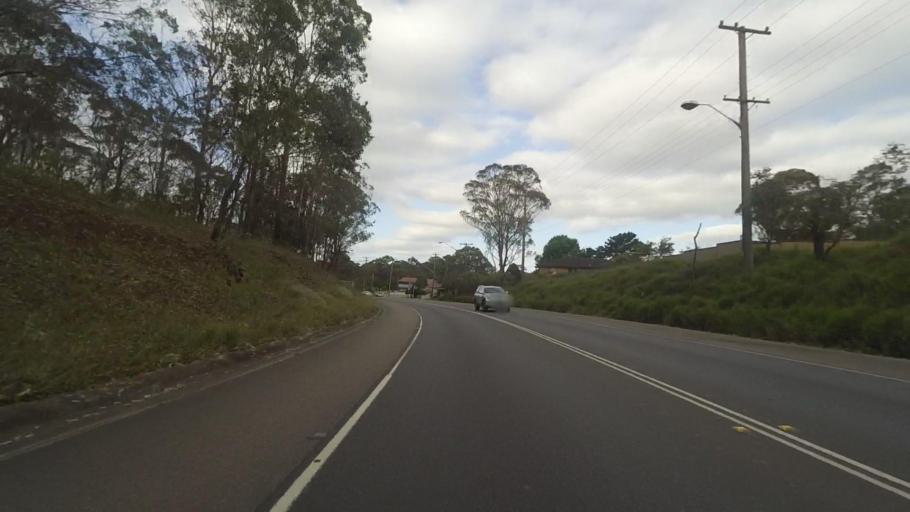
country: AU
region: New South Wales
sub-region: Bankstown
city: Milperra
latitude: -33.9097
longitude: 150.9808
